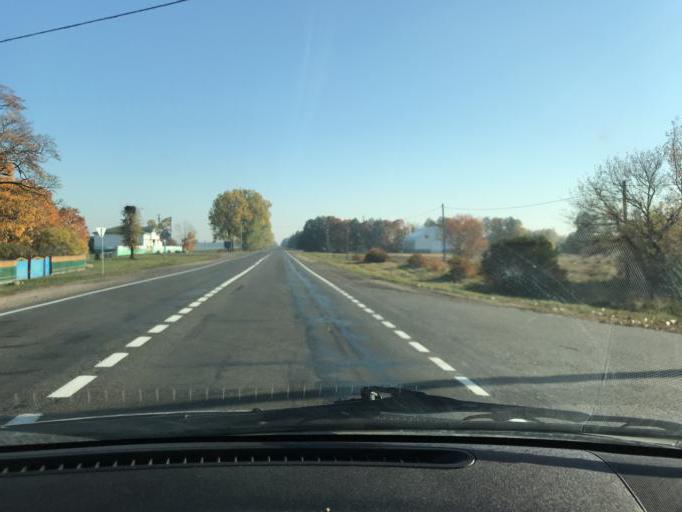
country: BY
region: Brest
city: Baranovichi
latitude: 52.8983
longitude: 25.8621
